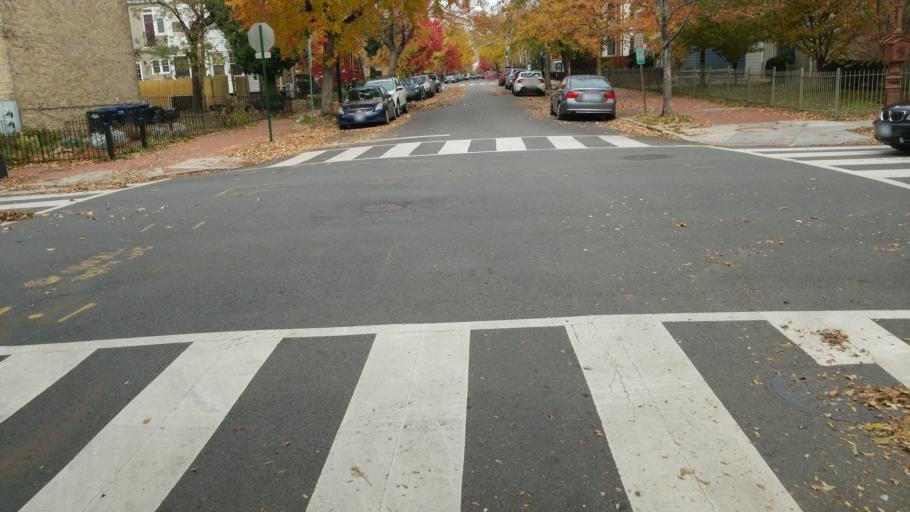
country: US
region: Washington, D.C.
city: Washington, D.C.
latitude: 38.8783
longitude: -76.9883
